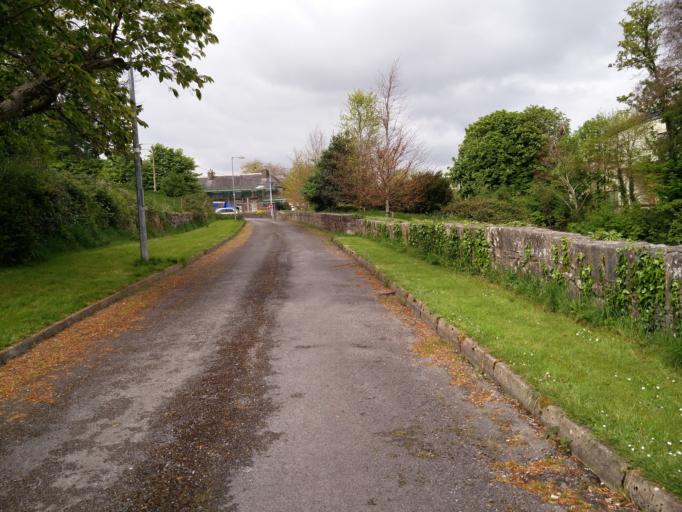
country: IE
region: Connaught
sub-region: Maigh Eo
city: Ballinrobe
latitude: 53.6236
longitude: -9.2249
